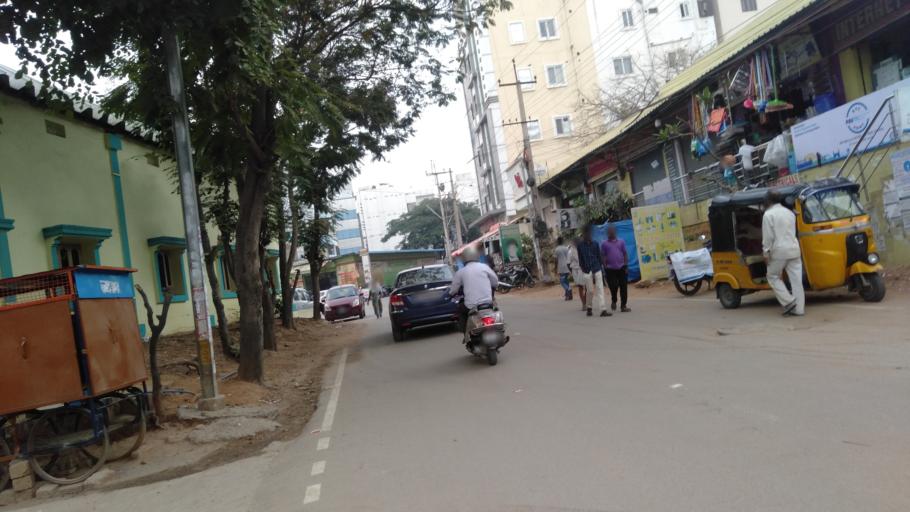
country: IN
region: Telangana
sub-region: Rangareddi
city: Kukatpalli
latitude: 17.4966
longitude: 78.3889
